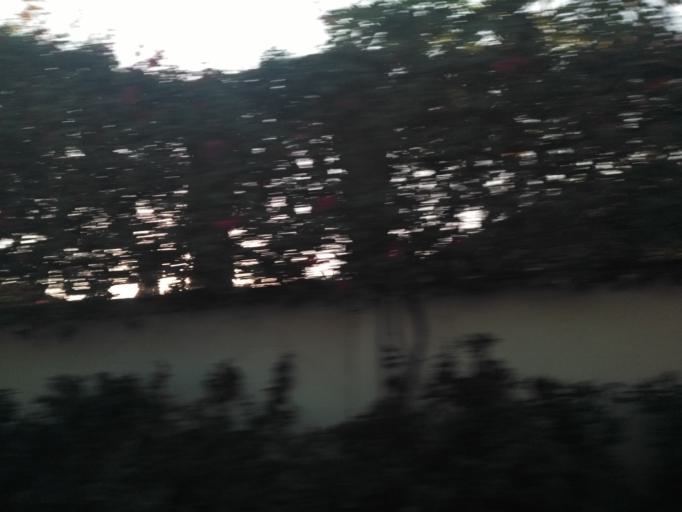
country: TZ
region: Dar es Salaam
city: Magomeni
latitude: -6.7649
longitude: 39.2500
